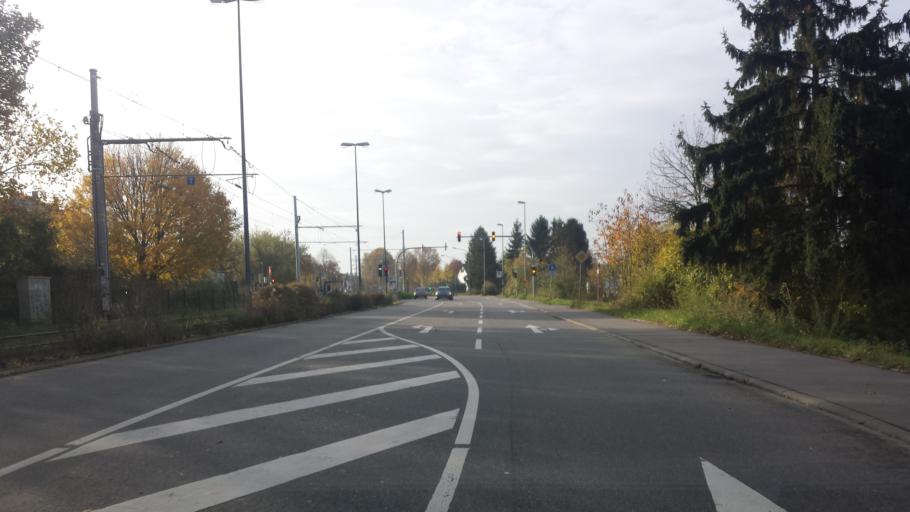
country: DE
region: Baden-Wuerttemberg
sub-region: Karlsruhe Region
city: Heidelberg
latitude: 49.3876
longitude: 8.6737
